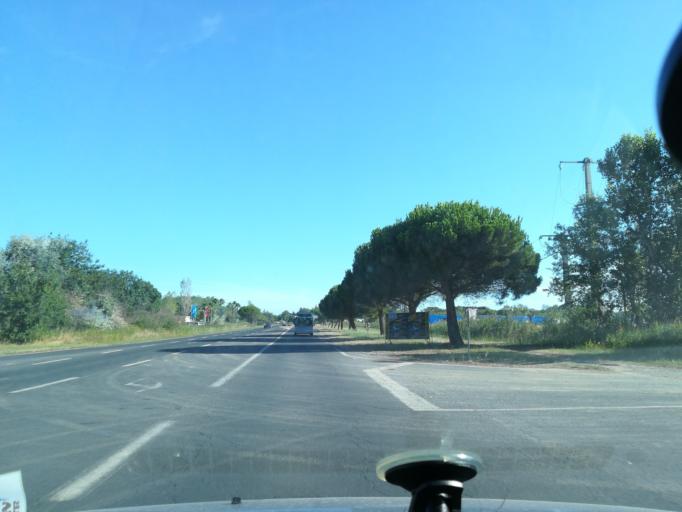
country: FR
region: Languedoc-Roussillon
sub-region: Departement de l'Herault
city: Portiragnes
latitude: 43.2862
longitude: 3.3627
